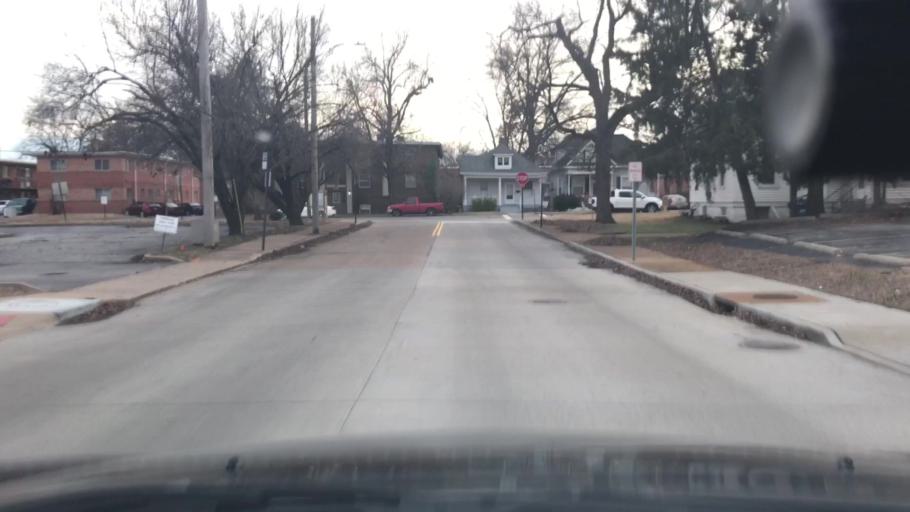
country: US
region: Missouri
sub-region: Saint Louis County
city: Maplewood
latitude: 38.6139
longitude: -90.3140
